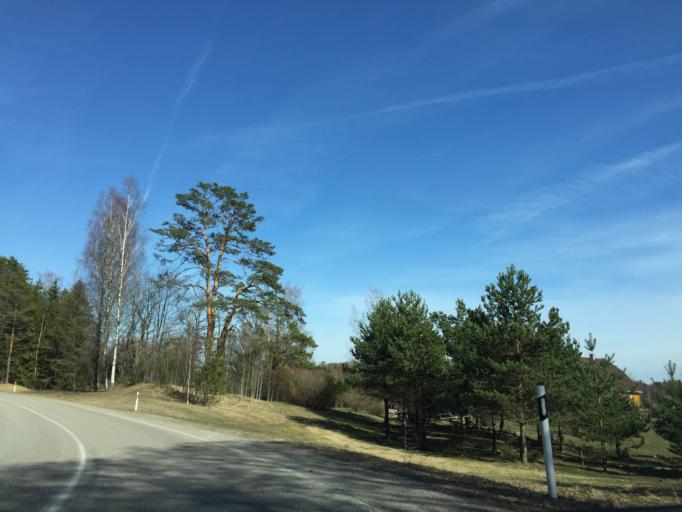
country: EE
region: Vorumaa
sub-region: Antsla vald
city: Vana-Antsla
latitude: 58.0093
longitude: 26.4180
